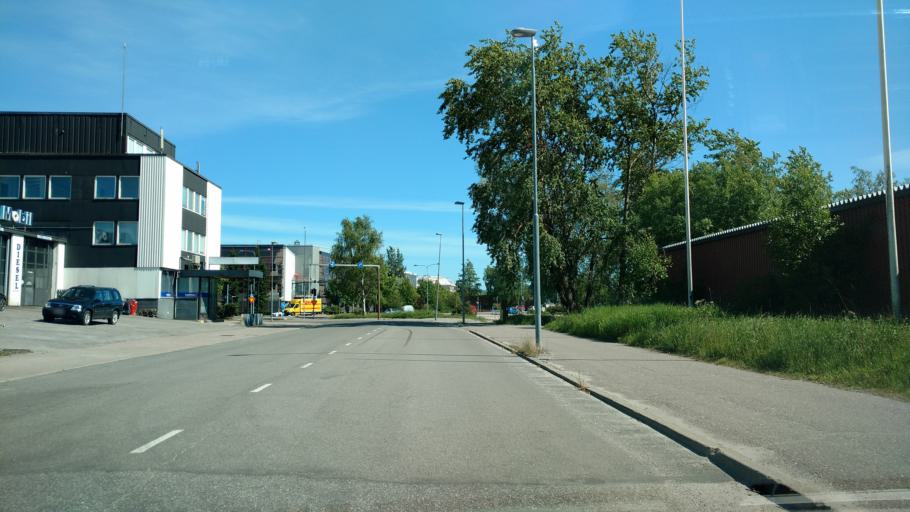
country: FI
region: Varsinais-Suomi
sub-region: Salo
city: Salo
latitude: 60.3901
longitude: 23.1151
